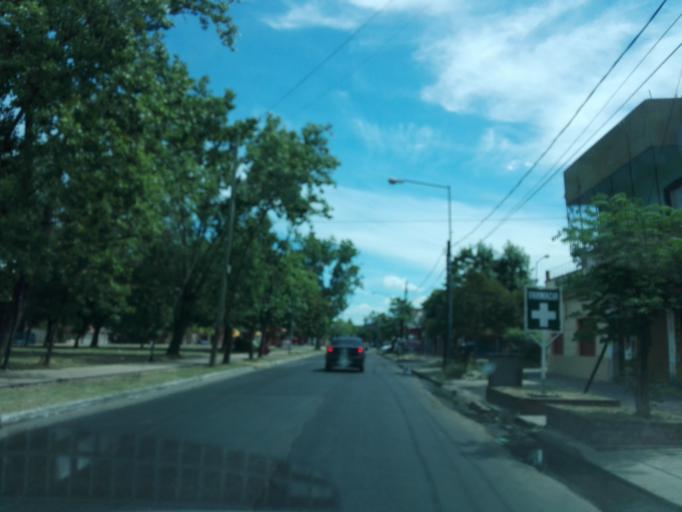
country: AR
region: Buenos Aires
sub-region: Partido de Lanus
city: Lanus
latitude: -34.7032
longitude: -58.3668
